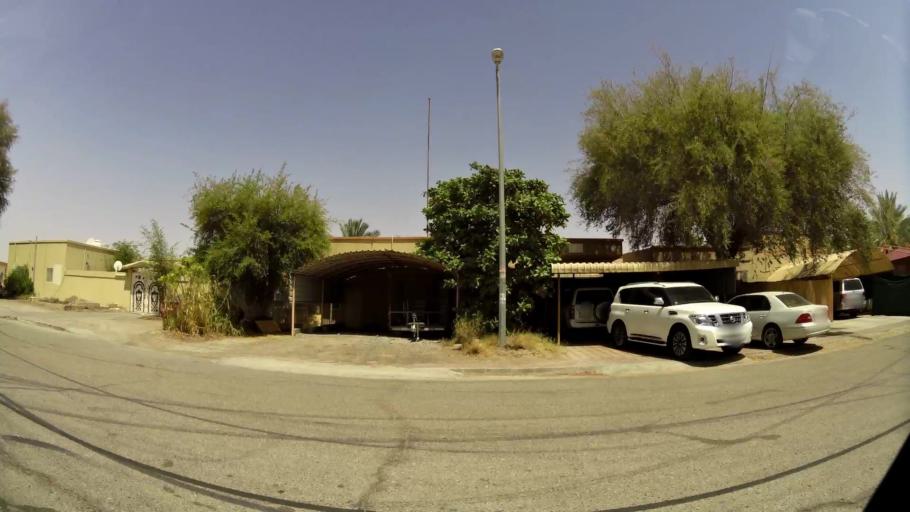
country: OM
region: Al Buraimi
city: Al Buraymi
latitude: 24.2847
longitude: 55.7641
